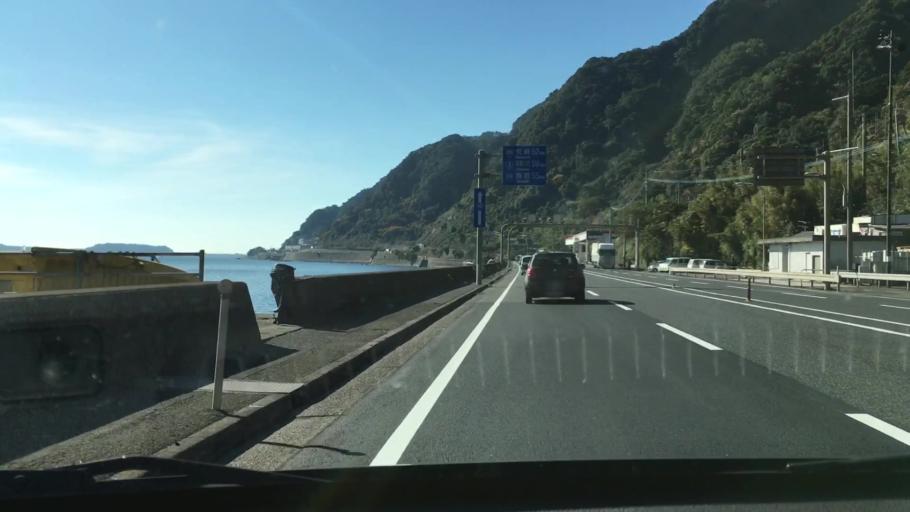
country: JP
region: Kagoshima
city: Kagoshima-shi
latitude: 31.6487
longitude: 130.6054
